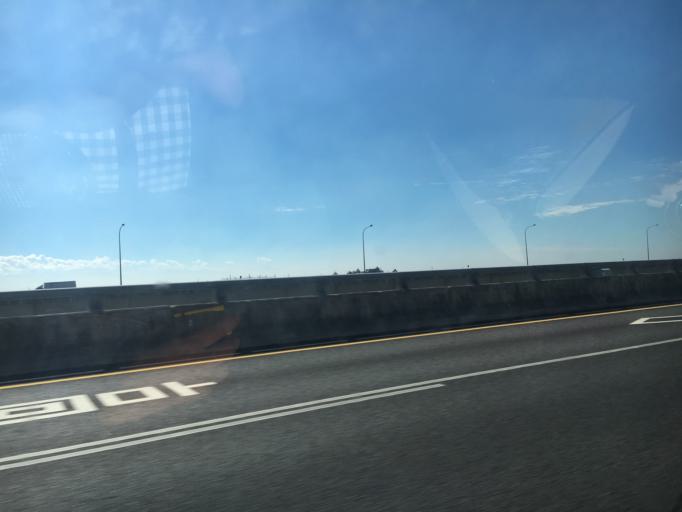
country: TW
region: Taiwan
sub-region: Taoyuan
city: Taoyuan
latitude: 25.0654
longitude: 121.3597
